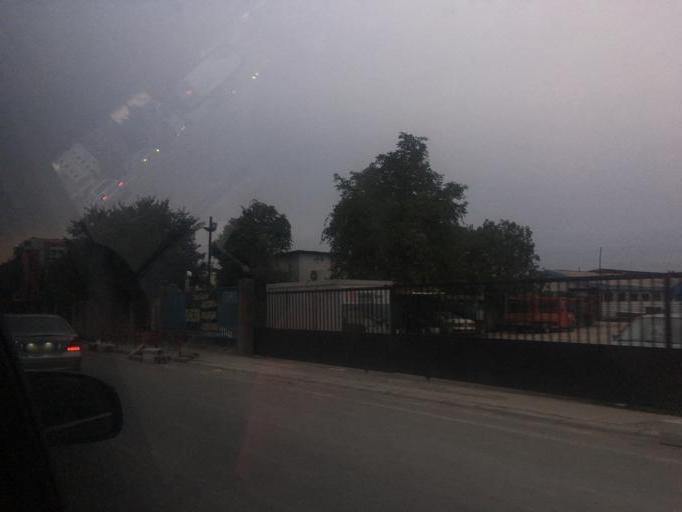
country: AL
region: Tirane
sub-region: Rrethi i Tiranes
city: Paskuqan
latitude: 41.3411
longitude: 19.7816
